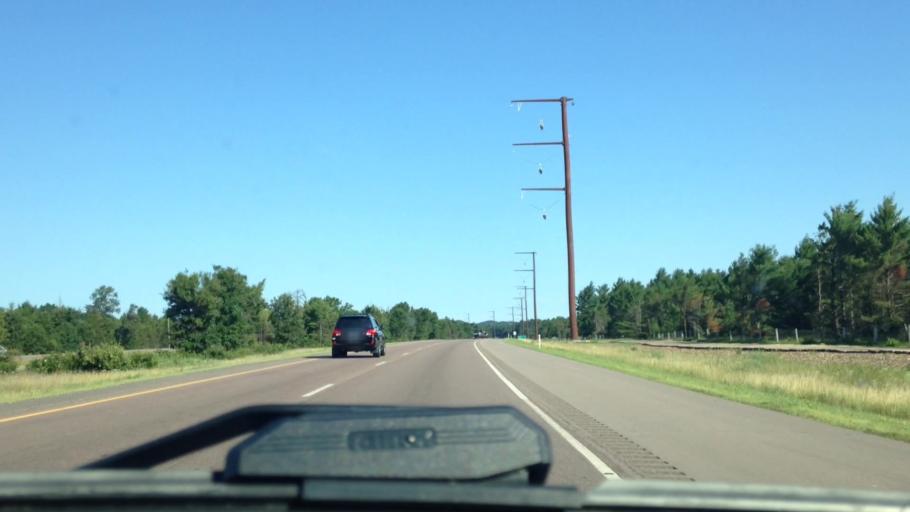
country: US
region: Wisconsin
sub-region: Jackson County
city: Black River Falls
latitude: 44.1981
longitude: -90.6505
